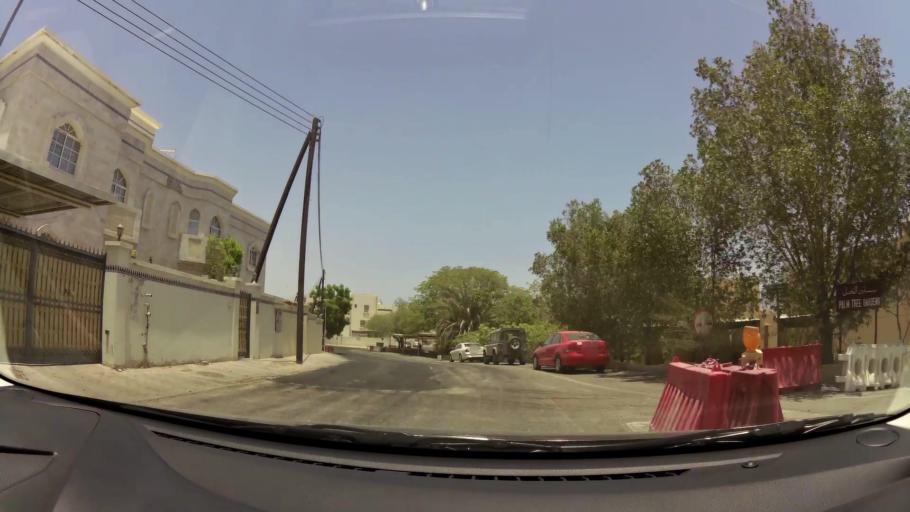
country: OM
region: Muhafazat Masqat
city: Bawshar
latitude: 23.6057
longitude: 58.4576
